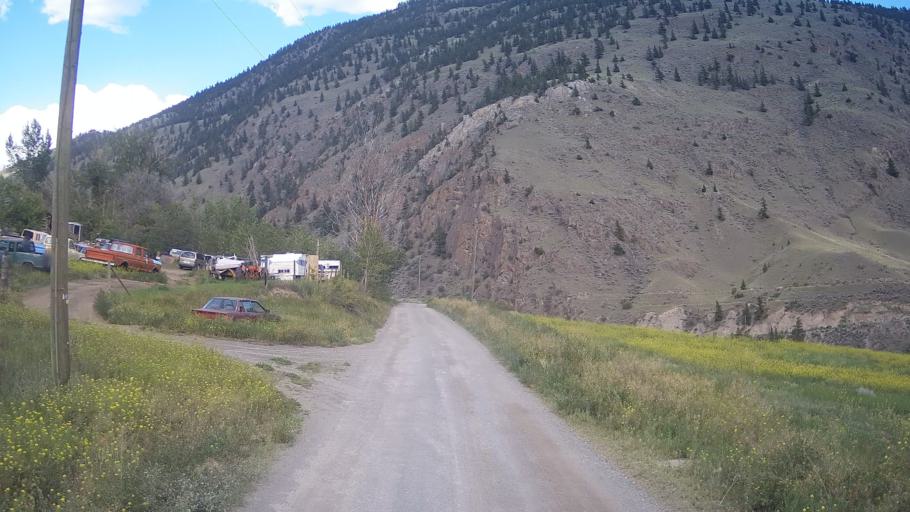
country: CA
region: British Columbia
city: Lillooet
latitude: 51.1976
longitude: -122.1068
